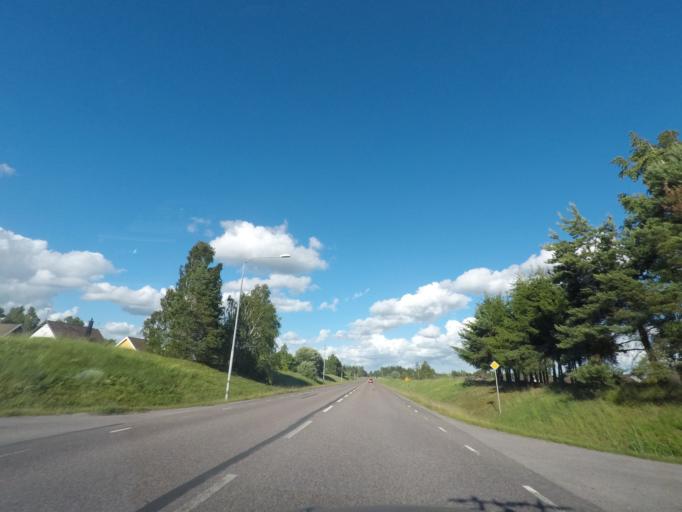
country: SE
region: Vaestmanland
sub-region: Arboga Kommun
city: Arboga
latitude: 59.4036
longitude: 15.8153
